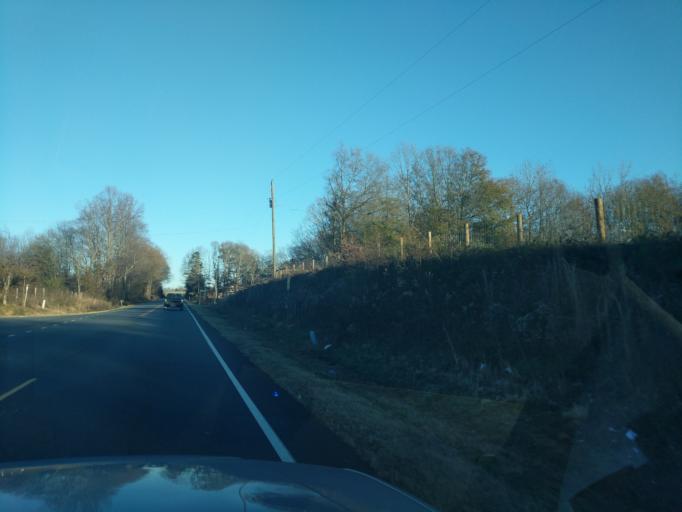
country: US
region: South Carolina
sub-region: Oconee County
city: Utica
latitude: 34.5843
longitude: -82.9332
